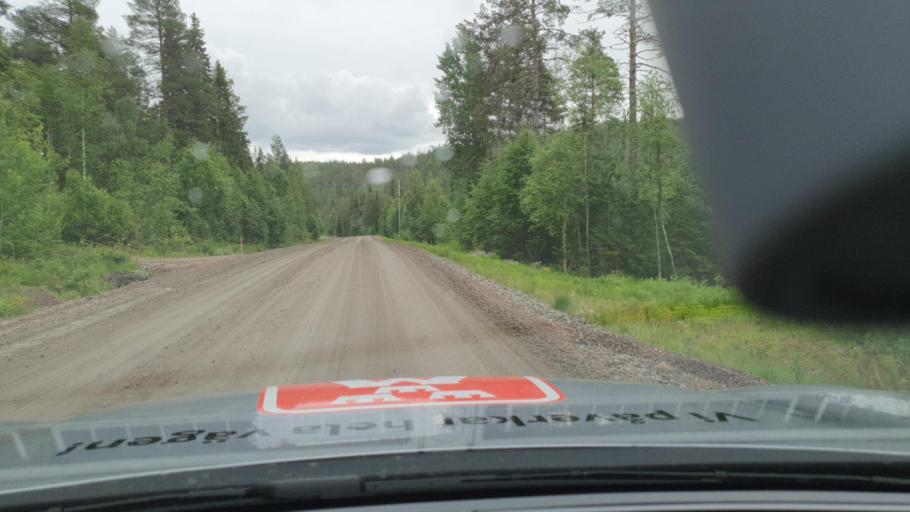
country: SE
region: Norrbotten
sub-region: Overtornea Kommun
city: OEvertornea
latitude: 66.4240
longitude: 23.5425
